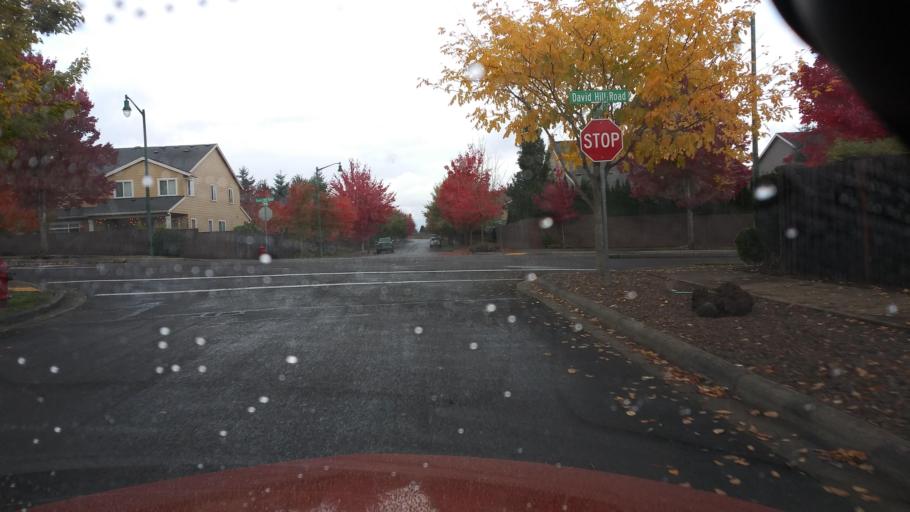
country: US
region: Oregon
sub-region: Washington County
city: Forest Grove
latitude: 45.5390
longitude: -123.1286
